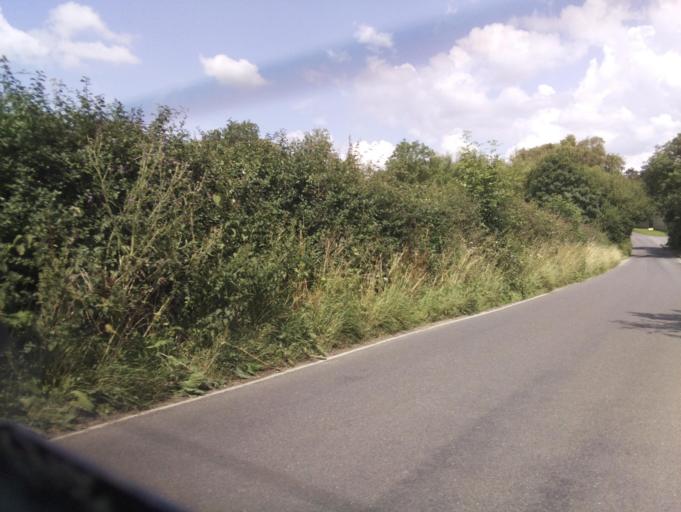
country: GB
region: England
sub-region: Wiltshire
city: Purton
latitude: 51.5823
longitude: -1.8641
